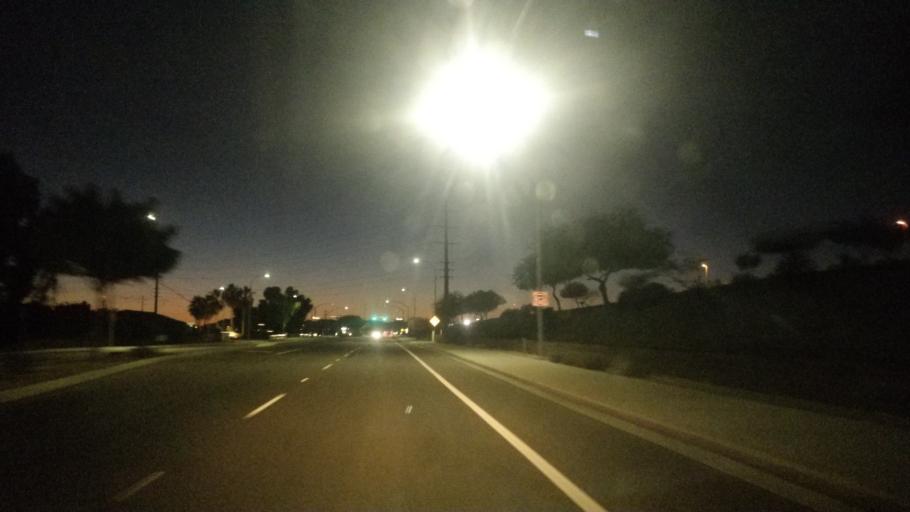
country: US
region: Arizona
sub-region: Maricopa County
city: Chandler
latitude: 33.2478
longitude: -111.8268
